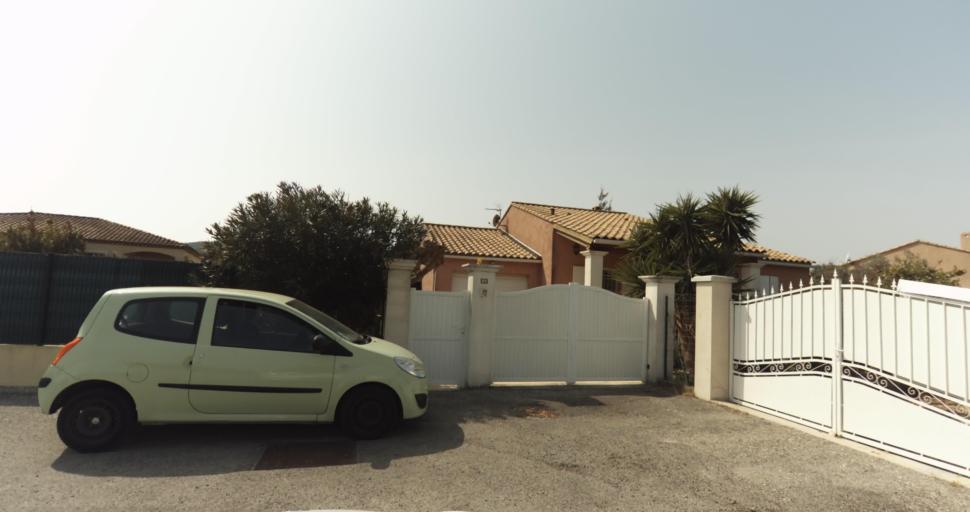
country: FR
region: Provence-Alpes-Cote d'Azur
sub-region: Departement du Var
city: Bormes-les-Mimosas
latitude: 43.1349
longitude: 6.3454
